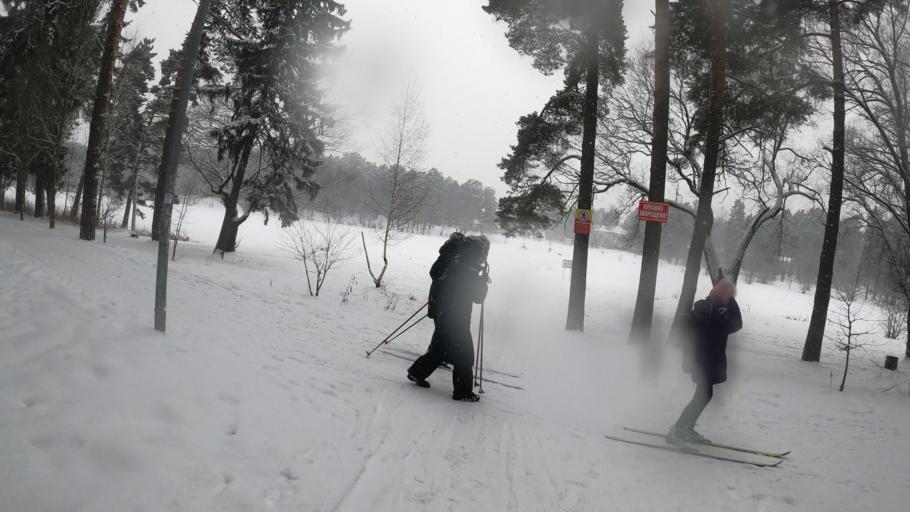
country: RU
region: Moskovskaya
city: Kratovo
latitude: 55.5878
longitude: 38.1610
